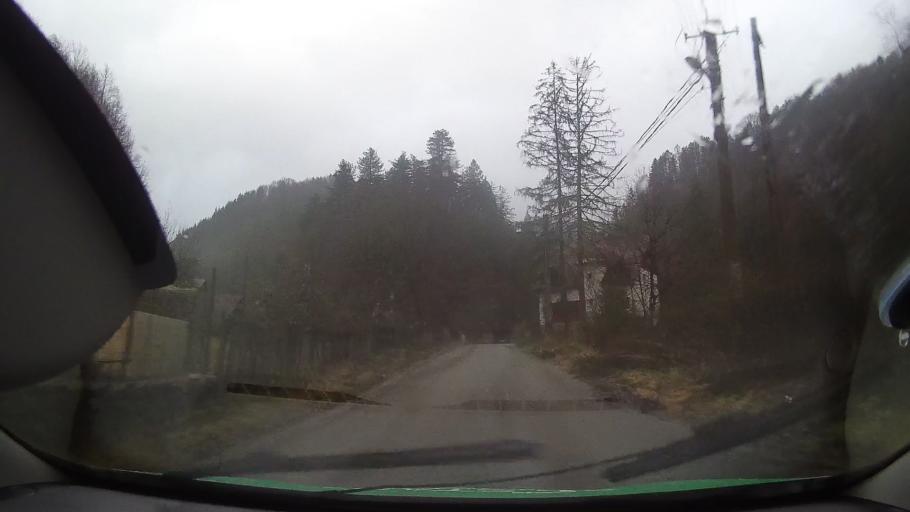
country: RO
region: Alba
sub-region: Comuna Avram Iancu
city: Avram Iancu
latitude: 46.3050
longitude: 22.7663
